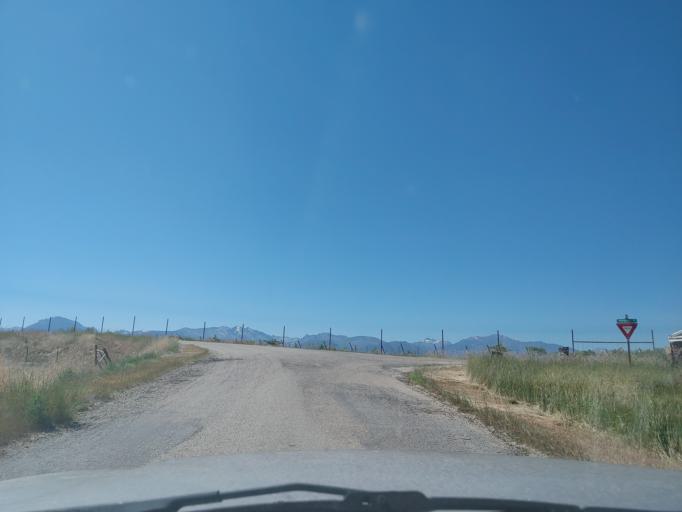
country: US
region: Montana
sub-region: Ravalli County
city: Hamilton
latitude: 46.3454
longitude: -114.0634
